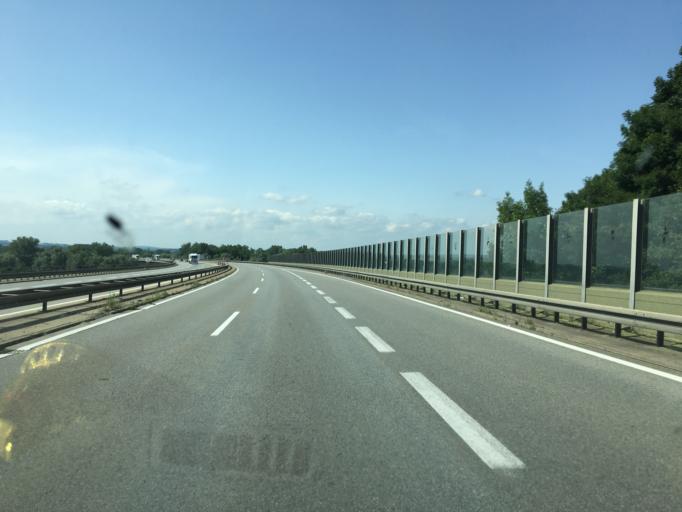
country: AT
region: Upper Austria
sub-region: Politischer Bezirk Scharding
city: Sankt Marienkirchen bei Schaerding
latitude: 48.4093
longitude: 13.4274
